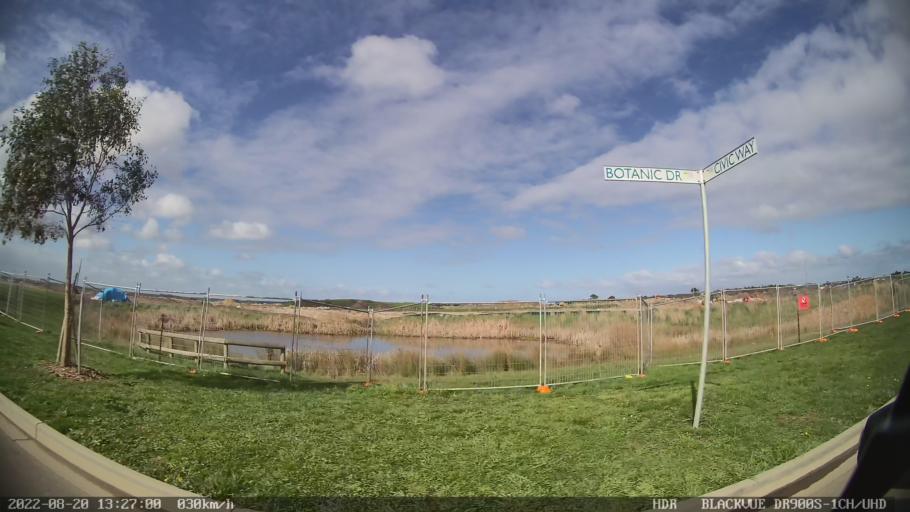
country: AU
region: Victoria
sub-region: Bass Coast
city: North Wonthaggi
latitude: -38.5981
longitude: 145.6107
